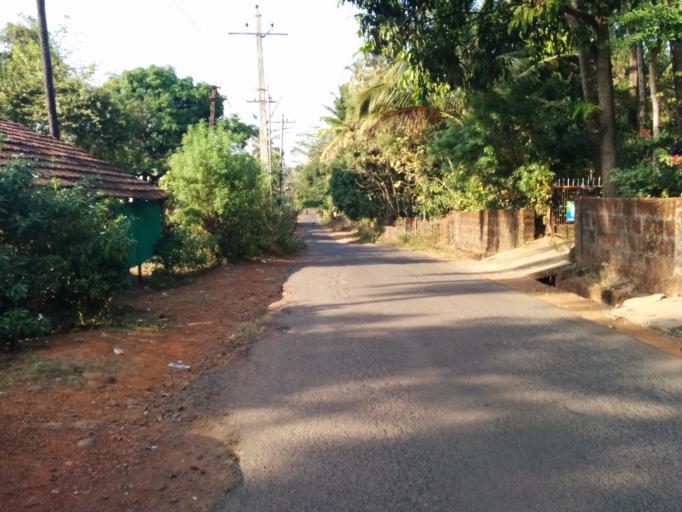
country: IN
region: Karnataka
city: Canacona
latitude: 15.0049
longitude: 74.0317
